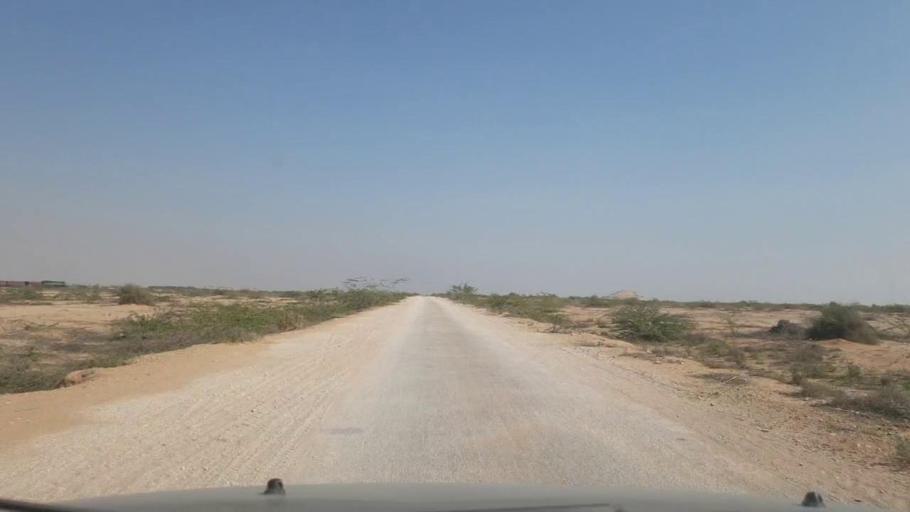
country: PK
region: Sindh
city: Thatta
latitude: 24.9776
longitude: 67.9791
